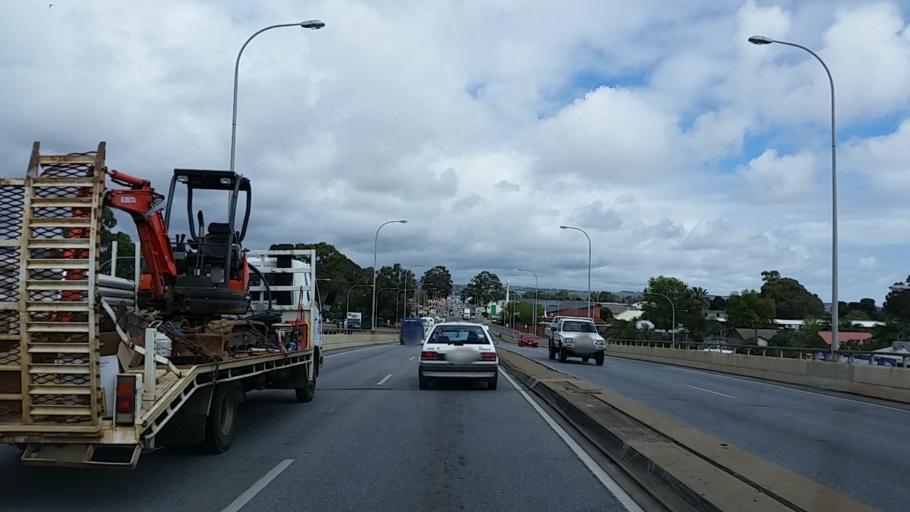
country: AU
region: South Australia
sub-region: Mitcham
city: Clarence Gardens
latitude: -34.9675
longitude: 138.5730
